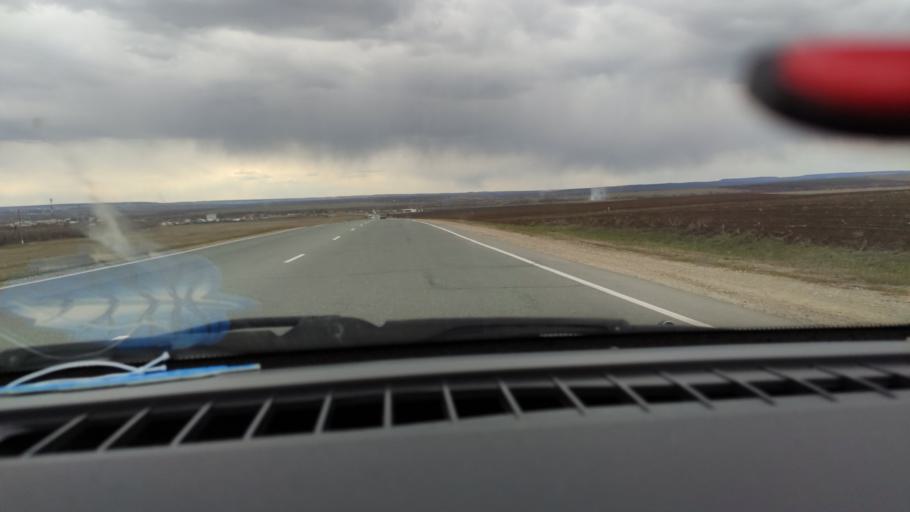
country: RU
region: Saratov
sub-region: Saratovskiy Rayon
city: Saratov
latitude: 51.7409
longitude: 46.0455
